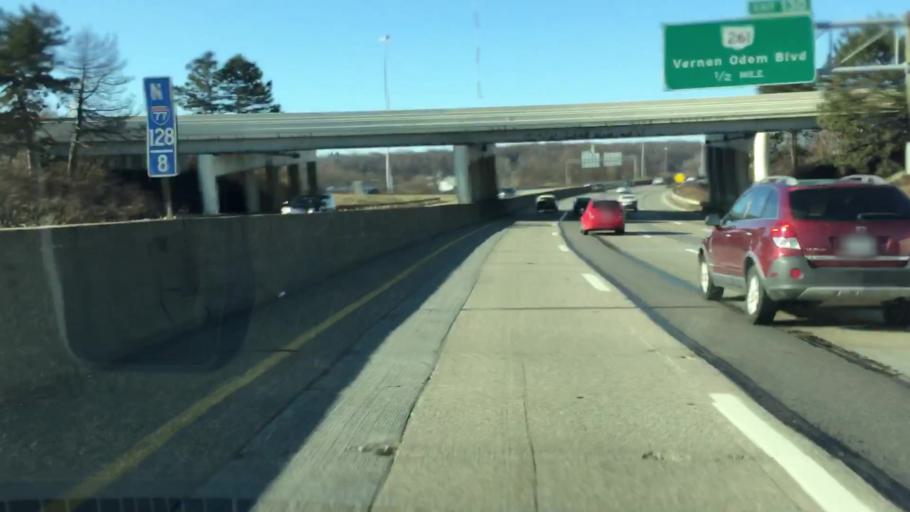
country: US
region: Ohio
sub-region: Summit County
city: Akron
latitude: 41.0608
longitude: -81.5673
